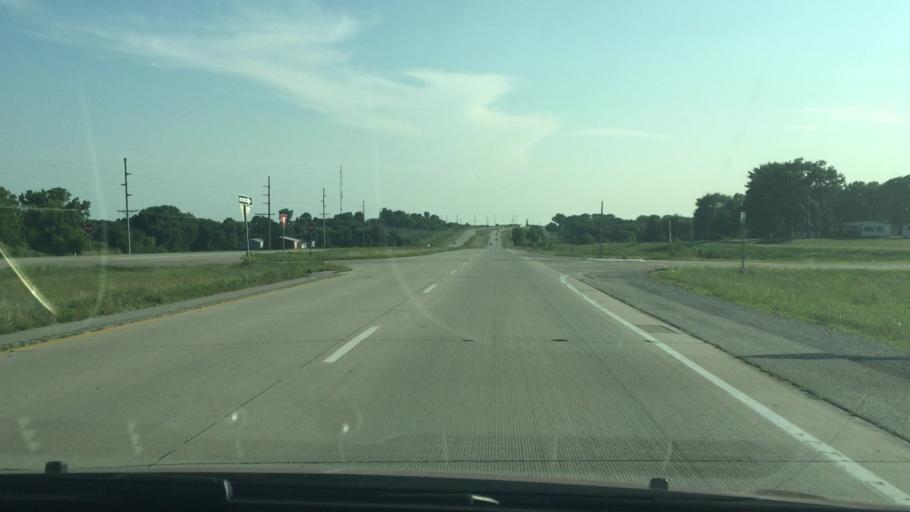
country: US
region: Iowa
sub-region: Muscatine County
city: Muscatine
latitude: 41.4744
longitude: -90.9990
